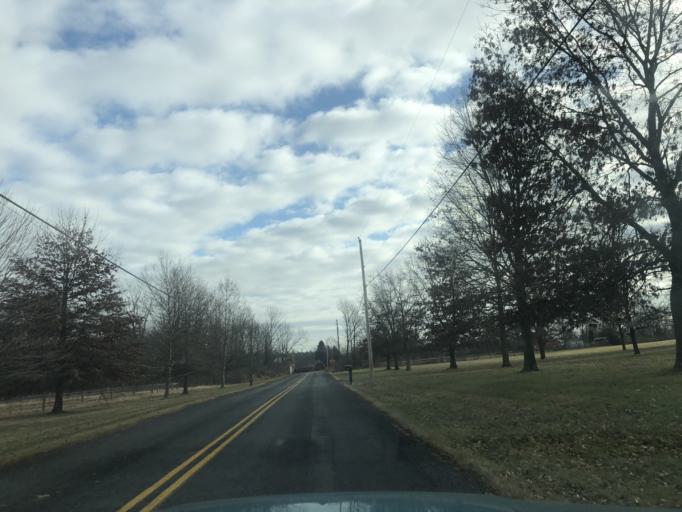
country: US
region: Pennsylvania
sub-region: Bucks County
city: Spinnerstown
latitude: 40.4448
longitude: -75.4182
